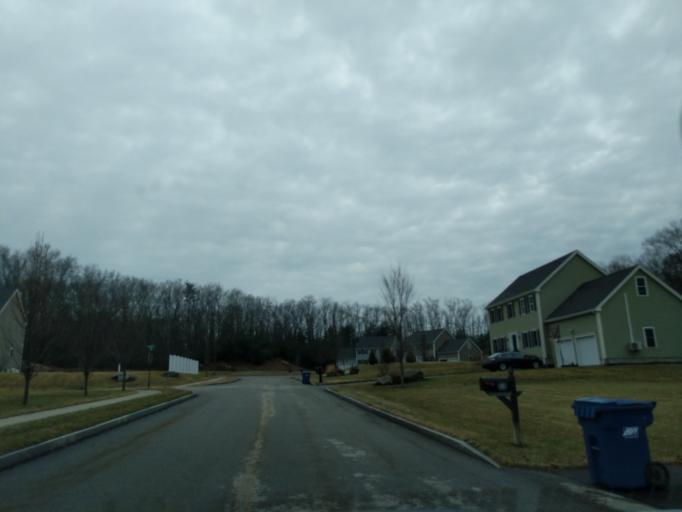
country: US
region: Massachusetts
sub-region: Worcester County
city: Whitinsville
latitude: 42.1040
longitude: -71.6920
